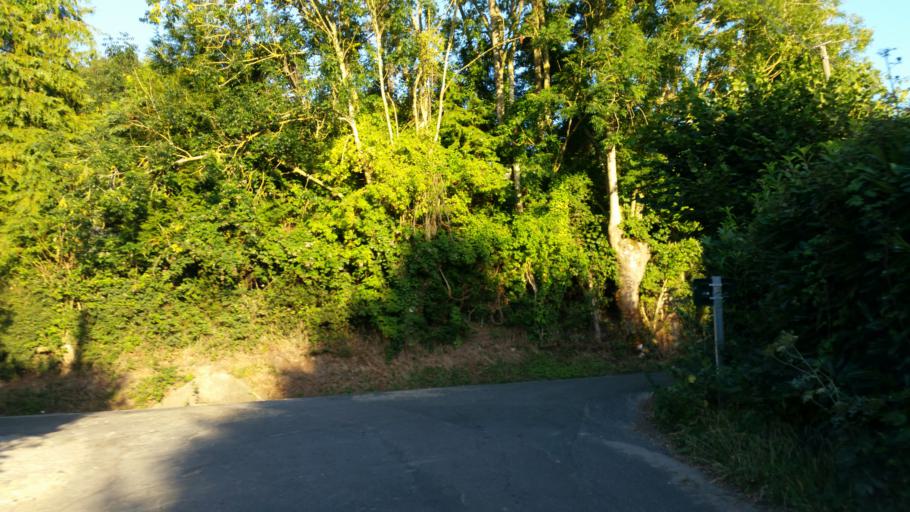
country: FR
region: Lower Normandy
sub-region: Departement du Calvados
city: Equemauville
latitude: 49.3982
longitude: 0.2239
